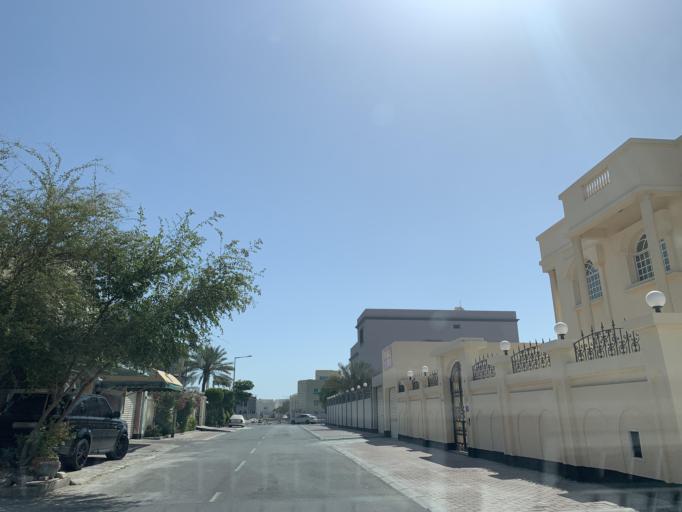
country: BH
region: Manama
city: Manama
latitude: 26.2010
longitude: 50.5664
